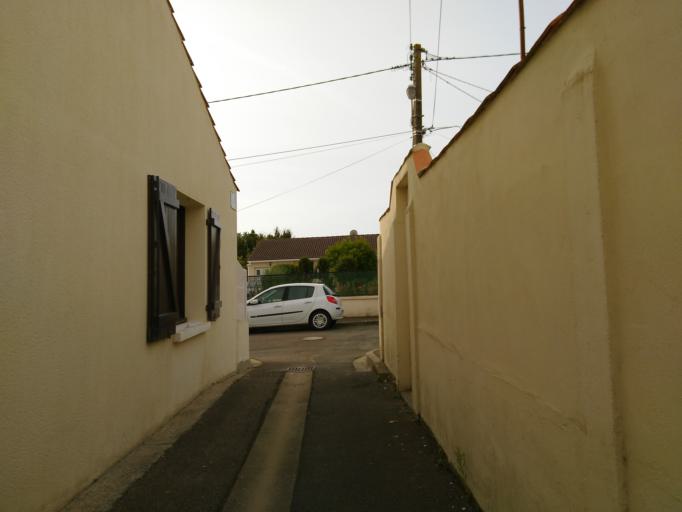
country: FR
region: Pays de la Loire
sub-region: Departement de la Vendee
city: Les Sables-d'Olonne
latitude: 46.4927
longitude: -1.7982
